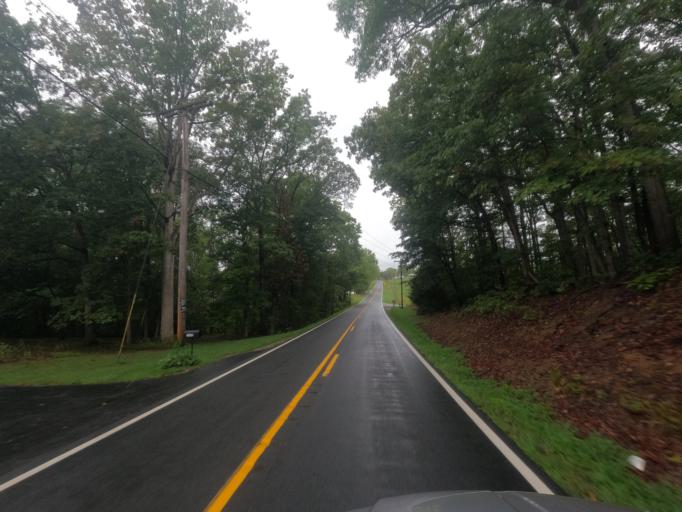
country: US
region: Maryland
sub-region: Washington County
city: Wilson-Conococheague
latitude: 39.6216
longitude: -77.9826
